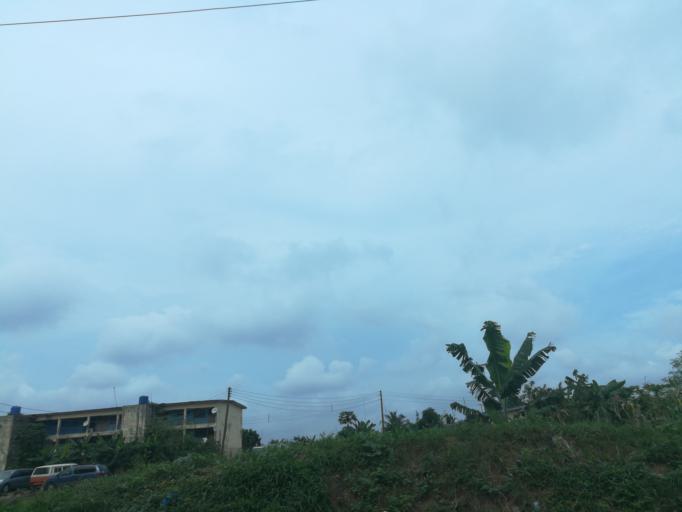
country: NG
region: Lagos
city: Oshodi
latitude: 6.5700
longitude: 3.3610
